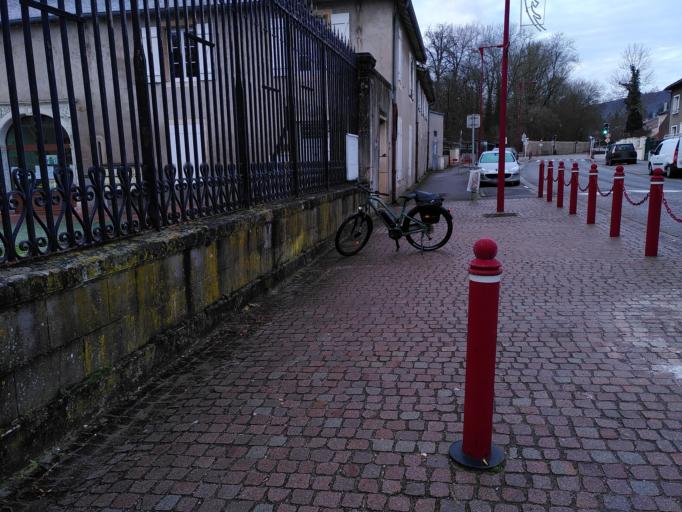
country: FR
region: Lorraine
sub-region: Departement de Meurthe-et-Moselle
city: Champigneulles
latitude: 48.7317
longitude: 6.1651
